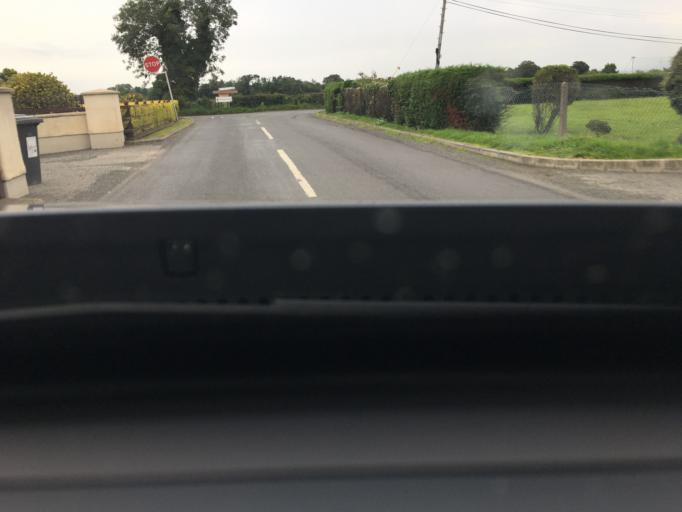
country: GB
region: Northern Ireland
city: Coalisland
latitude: 54.5357
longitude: -6.6172
